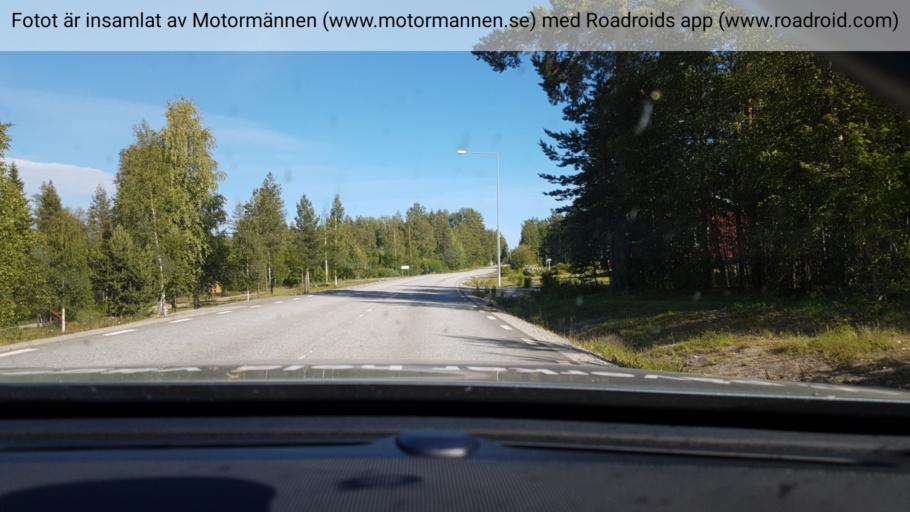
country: SE
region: Vaesterbotten
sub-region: Lycksele Kommun
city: Lycksele
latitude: 64.6380
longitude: 18.5303
